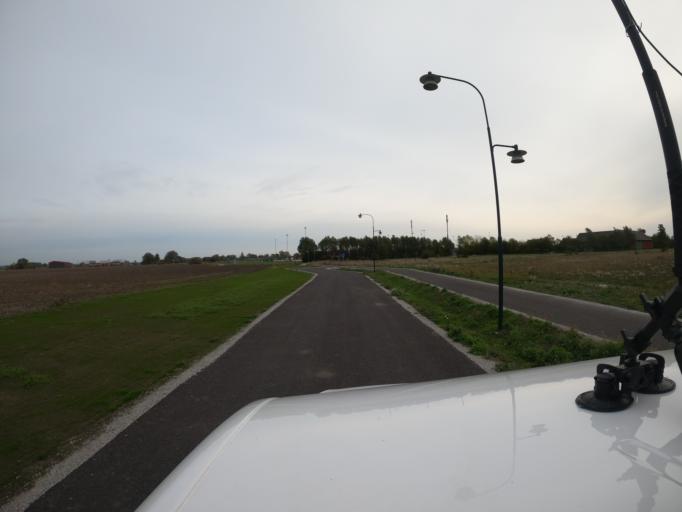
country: SE
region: Skane
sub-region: Lunds Kommun
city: Lund
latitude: 55.7511
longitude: 13.1907
